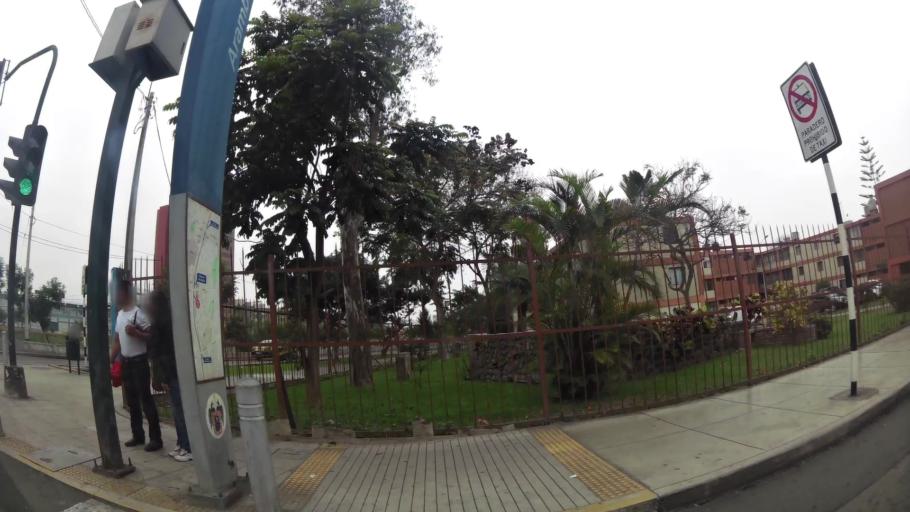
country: PE
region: Lima
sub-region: Lima
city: San Isidro
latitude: -12.1029
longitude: -77.0278
